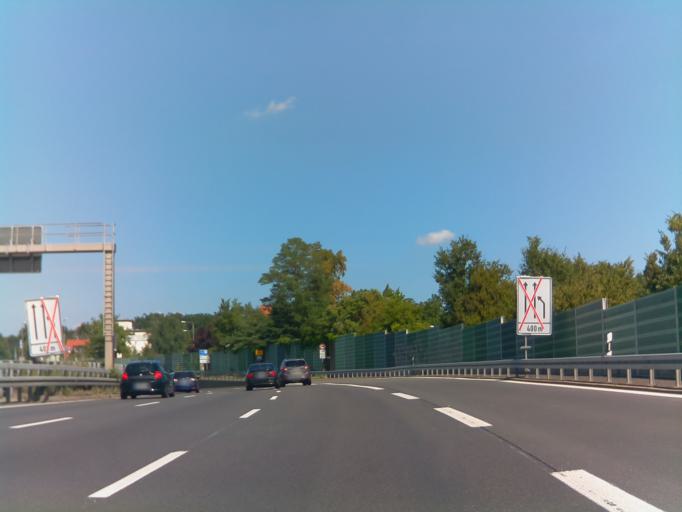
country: DE
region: Baden-Wuerttemberg
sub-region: Regierungsbezirk Stuttgart
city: Gerlingen
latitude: 48.7443
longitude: 9.1116
